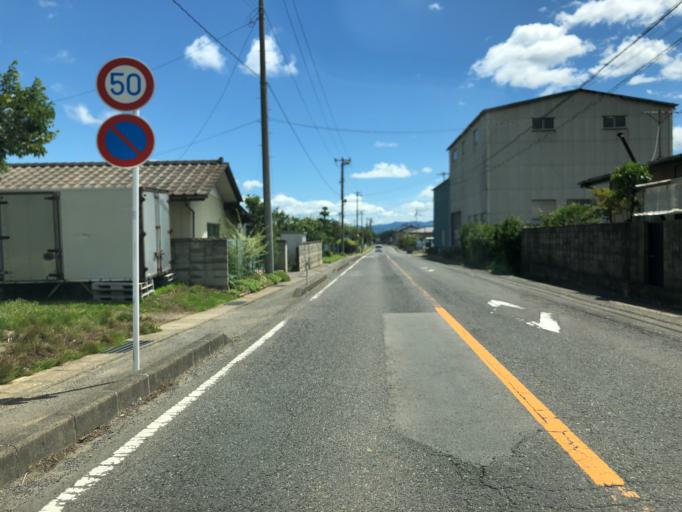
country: JP
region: Fukushima
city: Fukushima-shi
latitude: 37.7763
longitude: 140.3981
